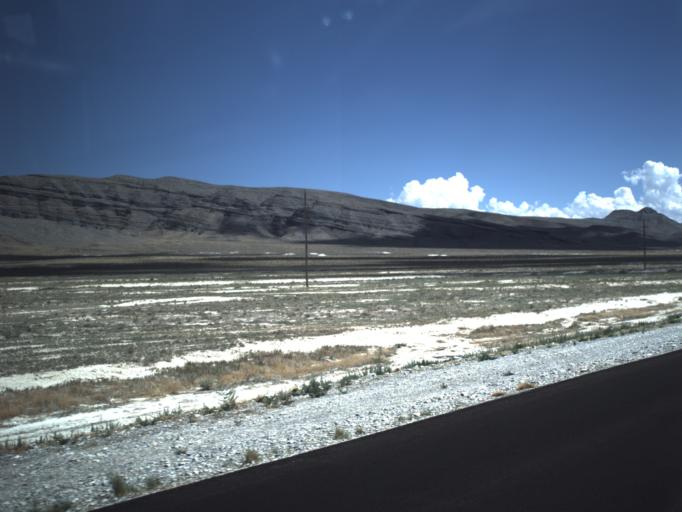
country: US
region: Utah
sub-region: Beaver County
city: Milford
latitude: 39.0626
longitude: -113.4422
